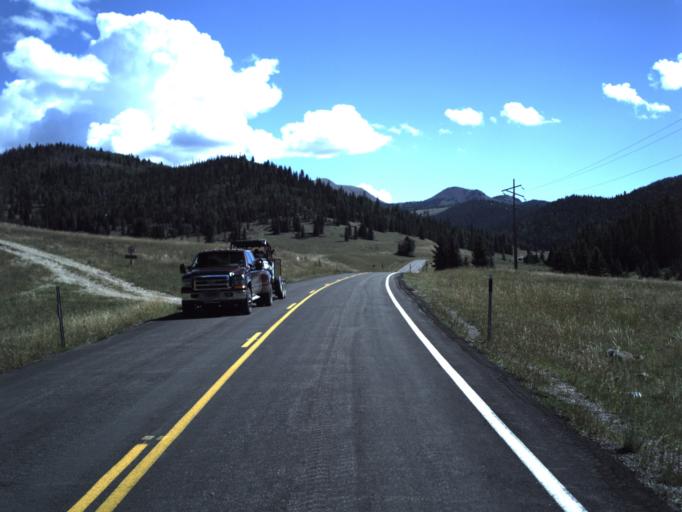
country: US
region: Utah
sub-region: Beaver County
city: Beaver
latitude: 38.2997
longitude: -112.4341
